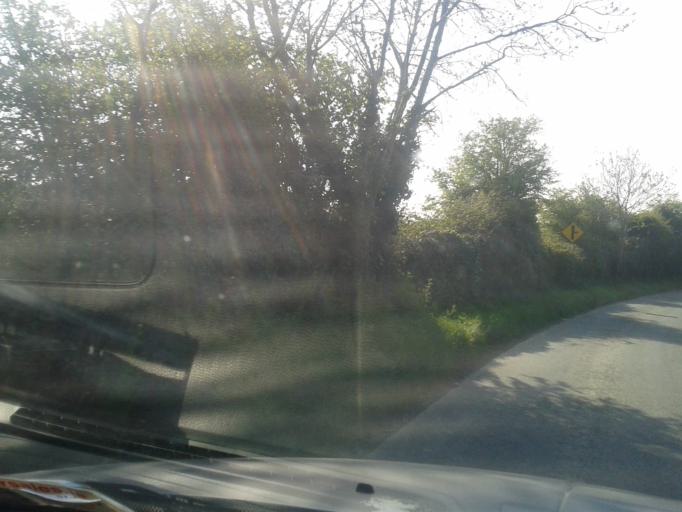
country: IE
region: Leinster
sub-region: Fingal County
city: Swords
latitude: 53.4739
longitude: -6.2215
